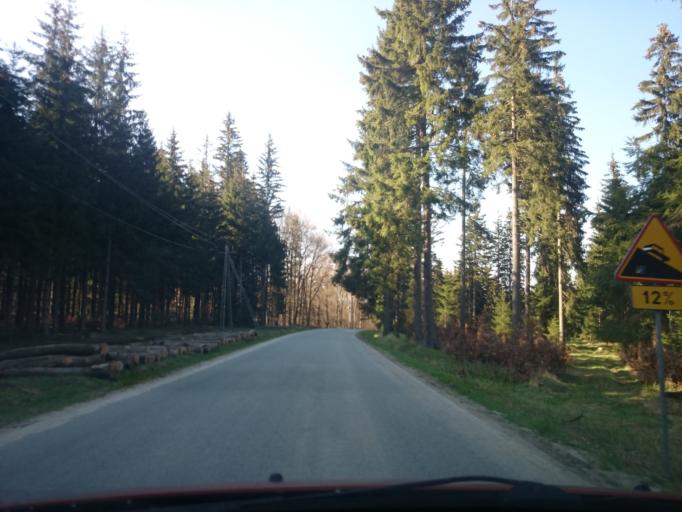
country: PL
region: Lower Silesian Voivodeship
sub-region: Powiat klodzki
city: Duszniki-Zdroj
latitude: 50.3318
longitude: 16.4054
